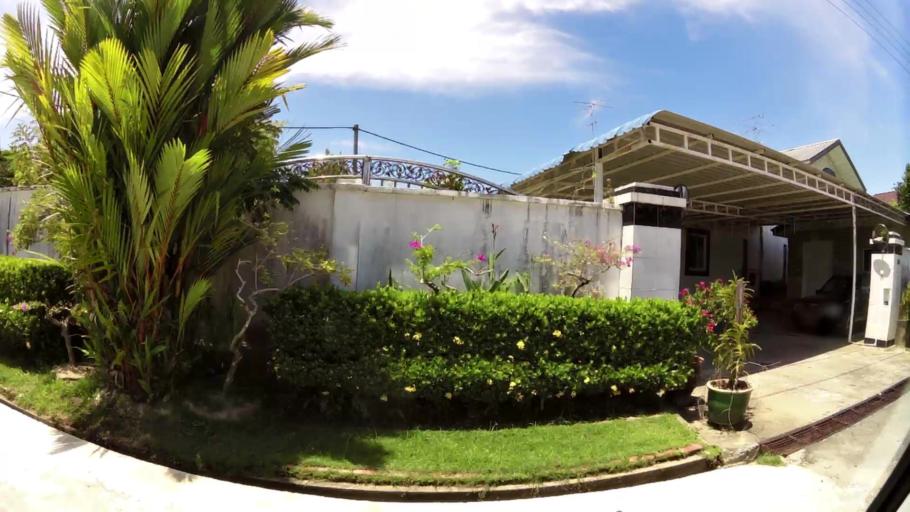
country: BN
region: Brunei and Muara
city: Bandar Seri Begawan
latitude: 4.9417
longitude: 114.9530
